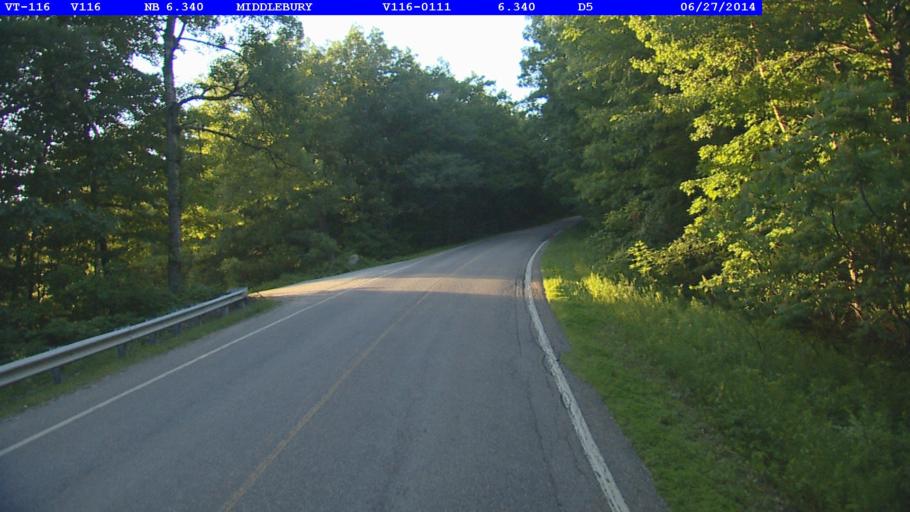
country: US
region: Vermont
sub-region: Addison County
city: Bristol
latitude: 44.0511
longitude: -73.0928
